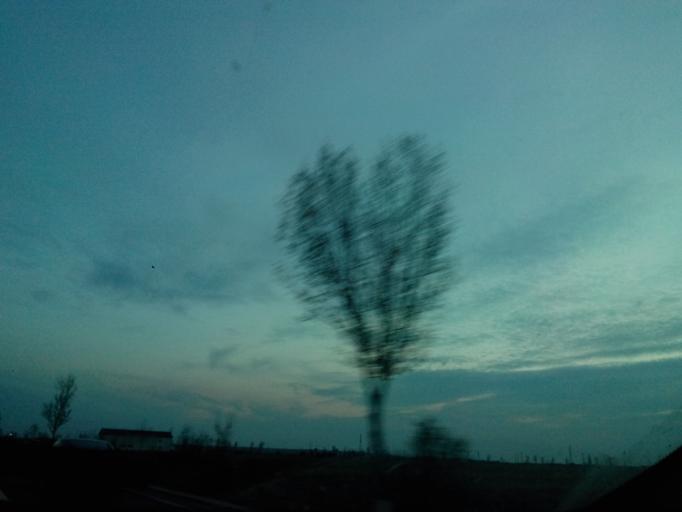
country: RO
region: Ilfov
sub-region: Comuna Balotesti
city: Balotesti
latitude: 44.6630
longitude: 26.0761
